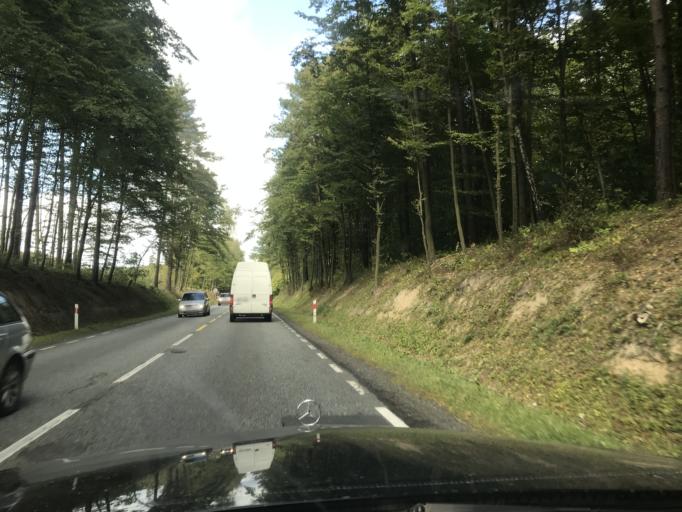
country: PL
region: Lublin Voivodeship
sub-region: Powiat krasnicki
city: Szastarka
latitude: 50.8508
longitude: 22.2888
